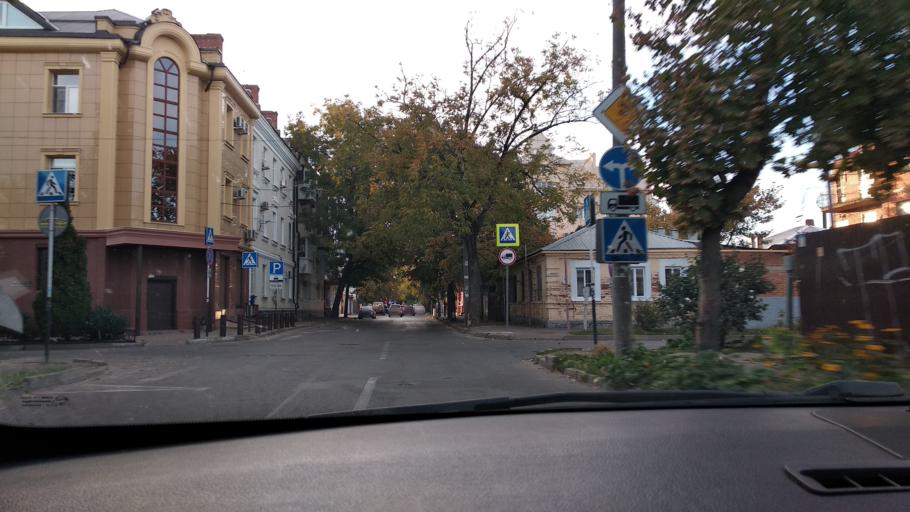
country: RU
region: Krasnodarskiy
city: Krasnodar
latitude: 45.0270
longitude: 38.9804
